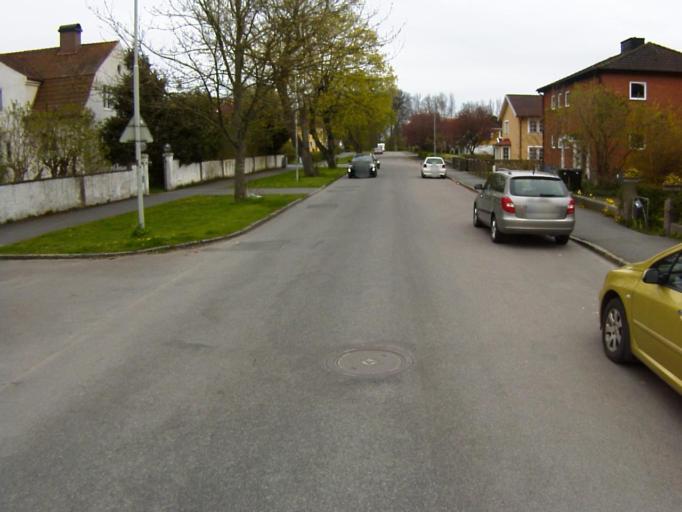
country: SE
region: Skane
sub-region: Kristianstads Kommun
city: Kristianstad
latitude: 56.0208
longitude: 14.1619
